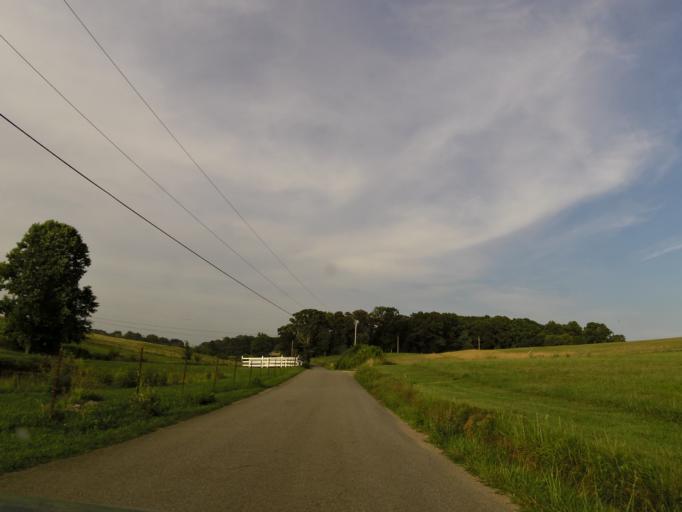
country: US
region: Tennessee
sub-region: Sevier County
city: Seymour
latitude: 35.8519
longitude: -83.7974
